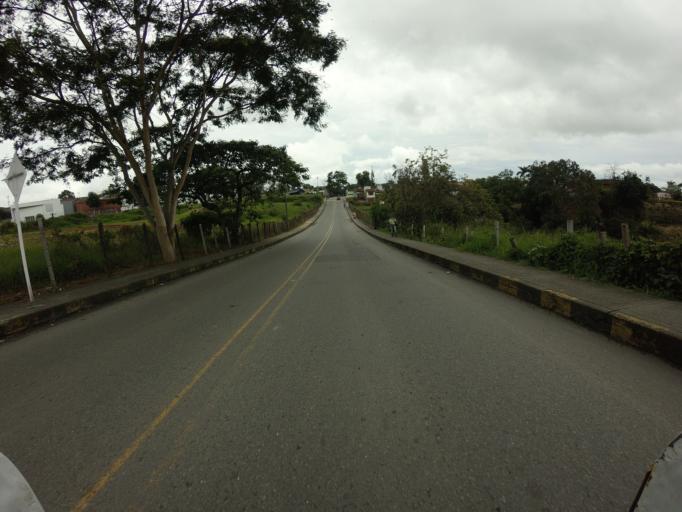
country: CO
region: Quindio
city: Quimbaya
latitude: 4.6219
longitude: -75.7676
